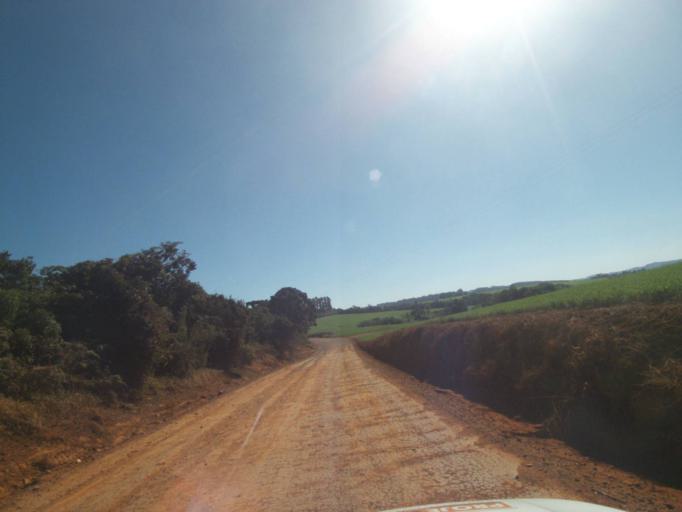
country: BR
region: Parana
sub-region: Reserva
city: Reserva
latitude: -24.6263
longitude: -50.6277
